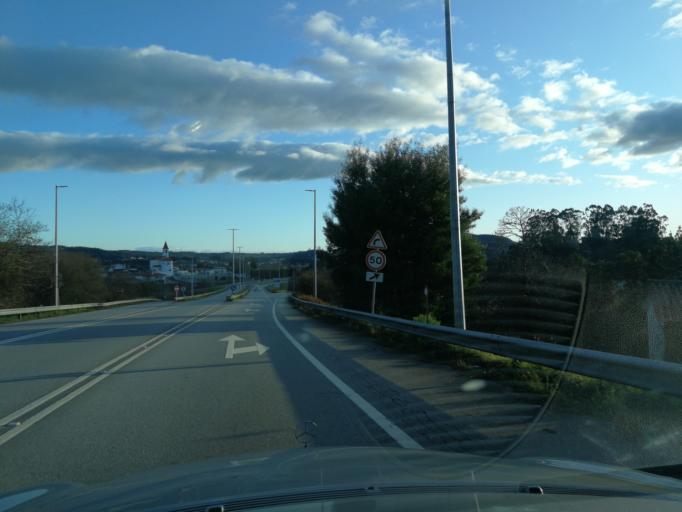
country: PT
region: Braga
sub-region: Barcelos
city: Vila Frescainha
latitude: 41.5375
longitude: -8.6389
